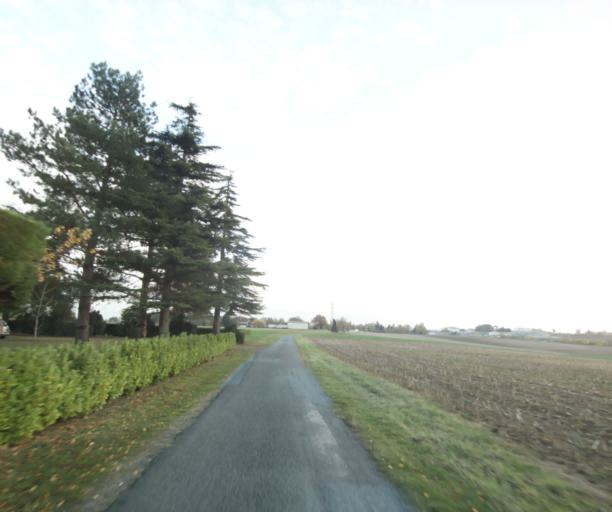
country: FR
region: Poitou-Charentes
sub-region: Departement de la Charente-Maritime
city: Bussac-sur-Charente
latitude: 45.7673
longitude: -0.6498
